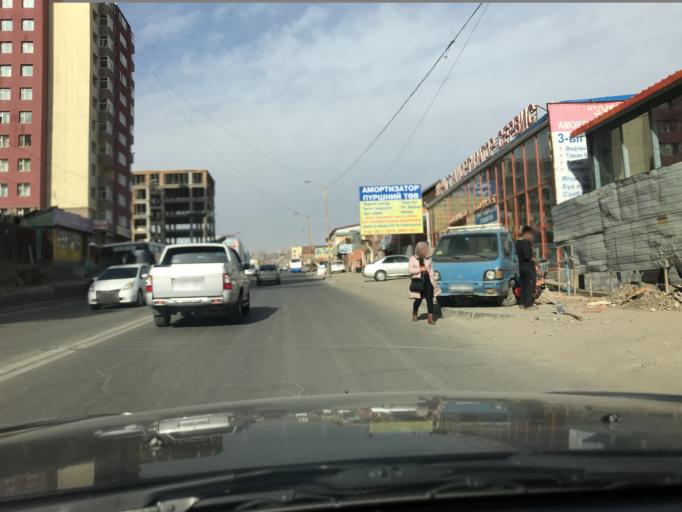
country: MN
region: Ulaanbaatar
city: Ulaanbaatar
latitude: 47.9262
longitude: 106.8946
